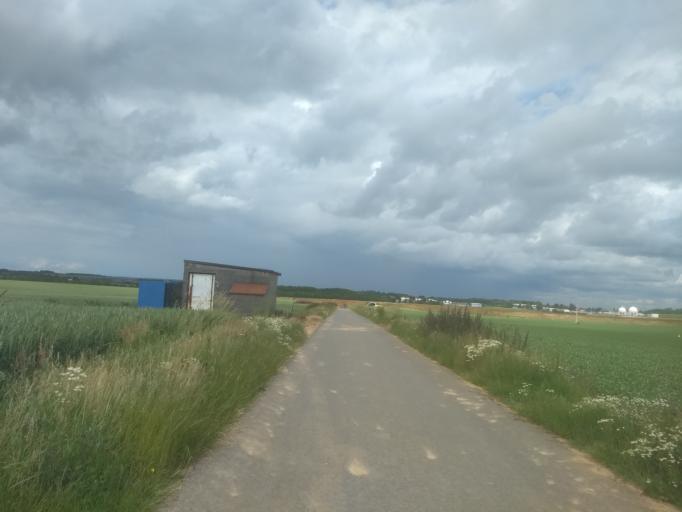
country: FR
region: Nord-Pas-de-Calais
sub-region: Departement du Pas-de-Calais
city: Dainville
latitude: 50.2617
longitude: 2.7079
